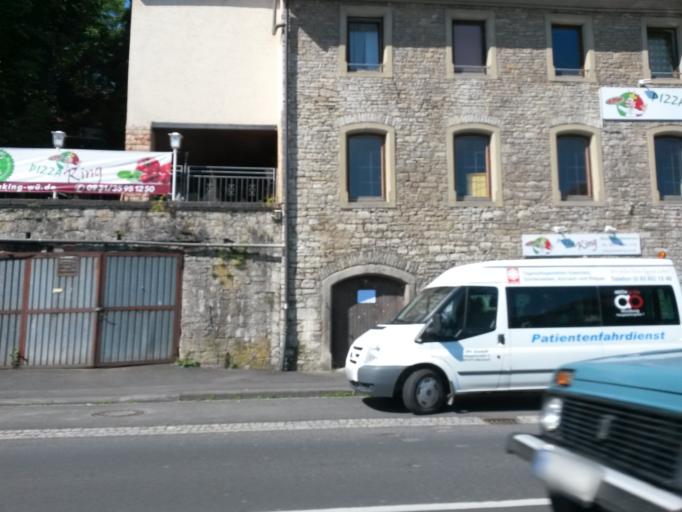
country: DE
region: Bavaria
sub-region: Regierungsbezirk Unterfranken
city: Wuerzburg
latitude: 49.8193
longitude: 9.9630
